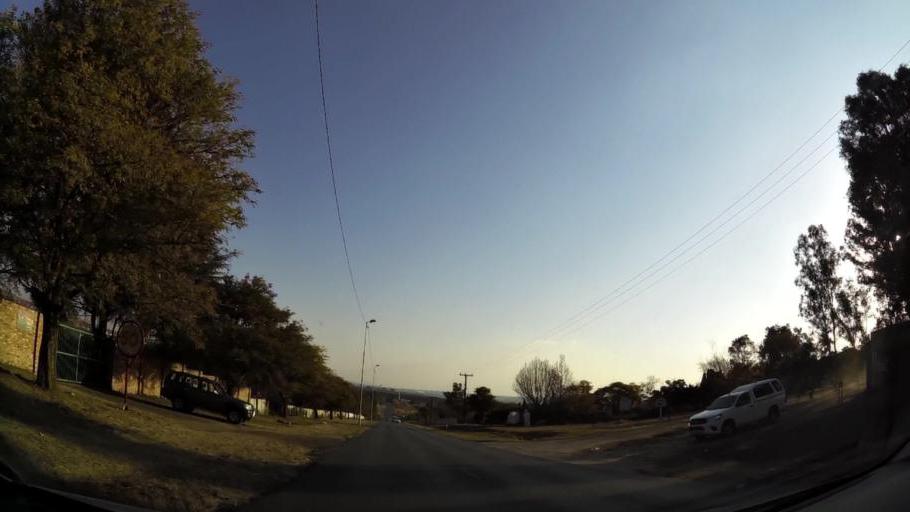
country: ZA
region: Gauteng
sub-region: City of Johannesburg Metropolitan Municipality
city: Midrand
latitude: -26.0286
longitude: 28.1441
